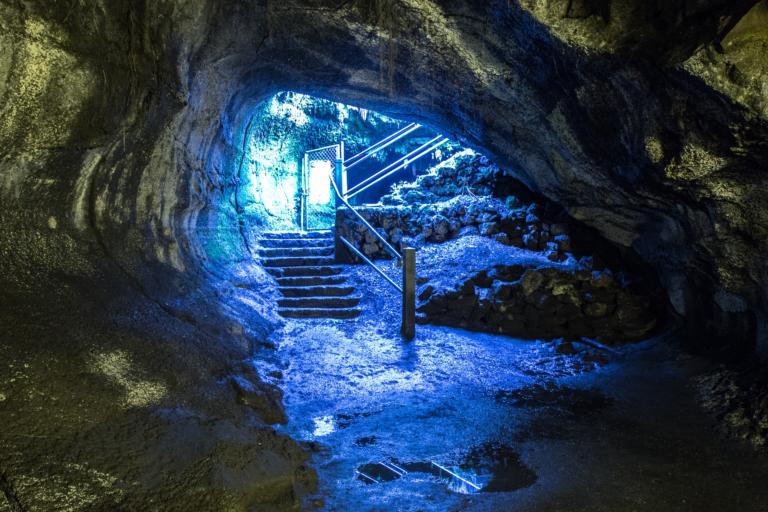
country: US
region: Hawaii
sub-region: Hawaii County
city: Volcano
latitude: 19.4150
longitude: -155.2370
